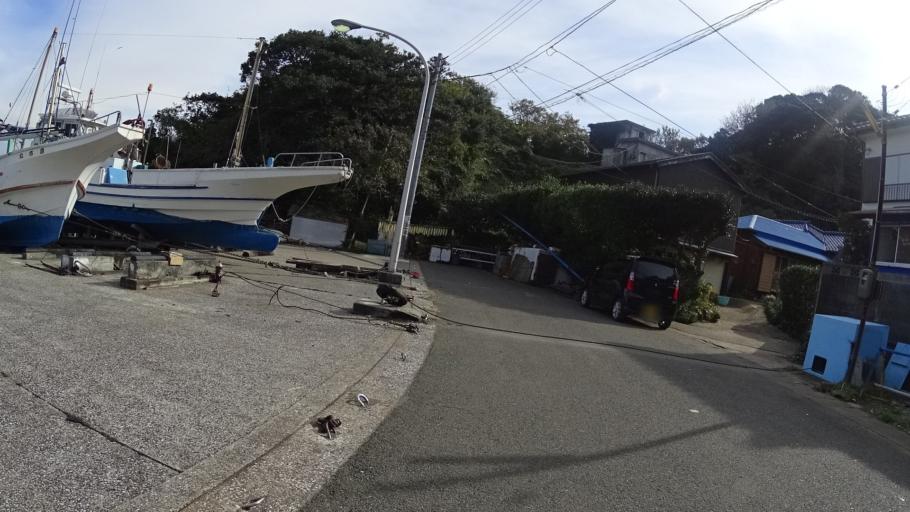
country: JP
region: Kanagawa
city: Miura
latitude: 35.1444
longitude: 139.6761
